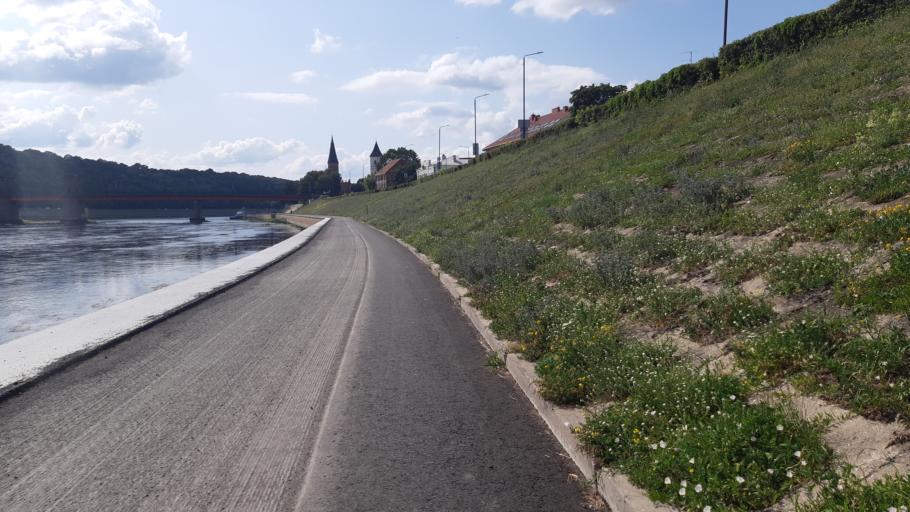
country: LT
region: Kauno apskritis
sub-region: Kaunas
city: Kaunas
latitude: 54.8946
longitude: 23.8935
